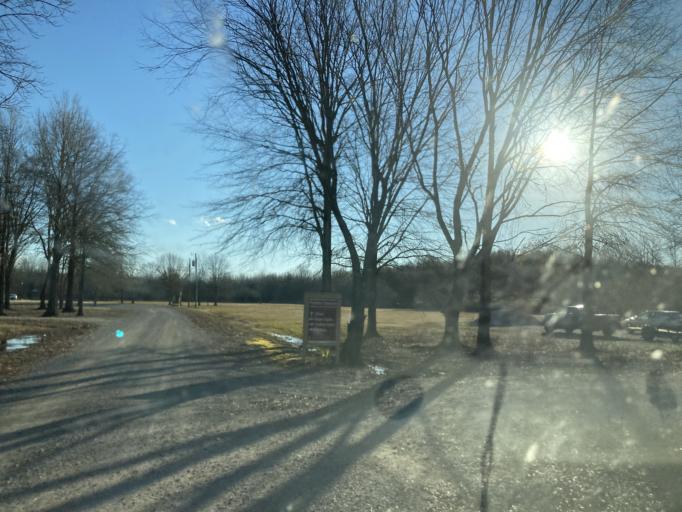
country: US
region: Mississippi
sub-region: Yazoo County
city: Yazoo City
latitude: 32.9238
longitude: -90.5744
